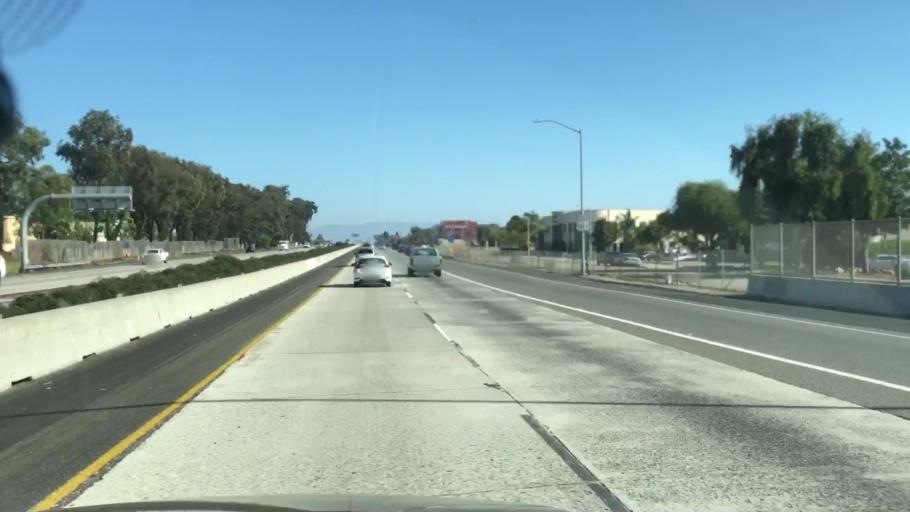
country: US
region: California
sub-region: Ventura County
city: Ventura
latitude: 34.2612
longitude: -119.2287
